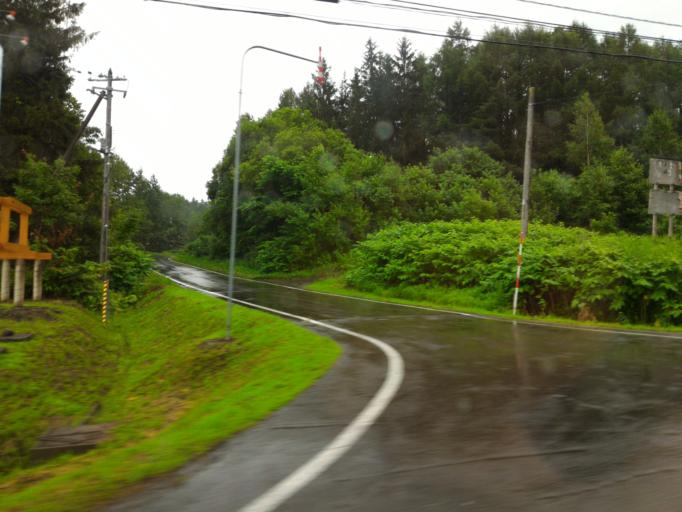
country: JP
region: Hokkaido
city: Nayoro
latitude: 44.6669
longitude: 142.2683
